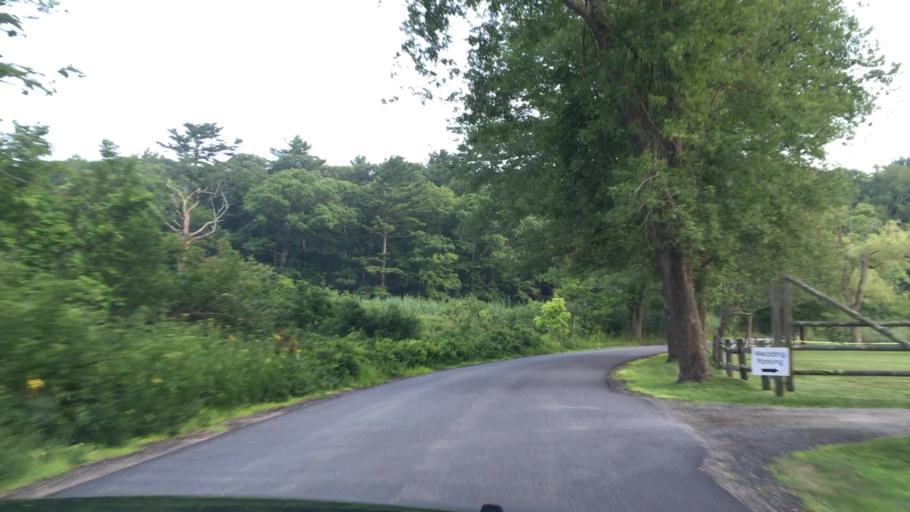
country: US
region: Massachusetts
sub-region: Essex County
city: Gloucester
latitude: 42.5775
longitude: -70.7259
